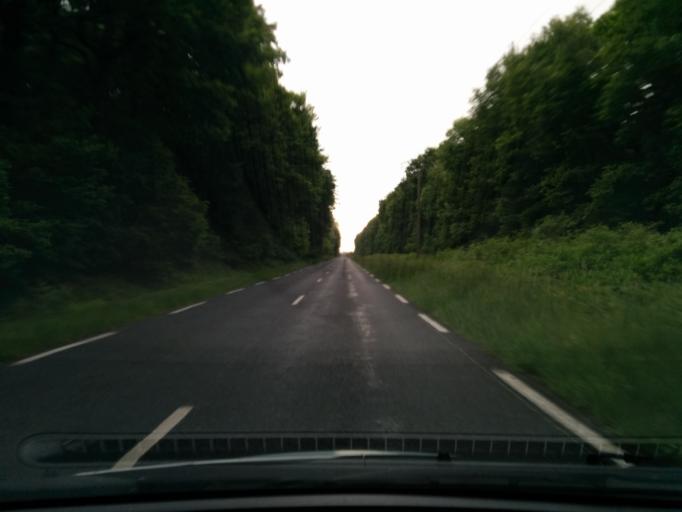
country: FR
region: Ile-de-France
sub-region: Departement des Yvelines
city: Limetz-Villez
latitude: 49.0967
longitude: 1.5172
